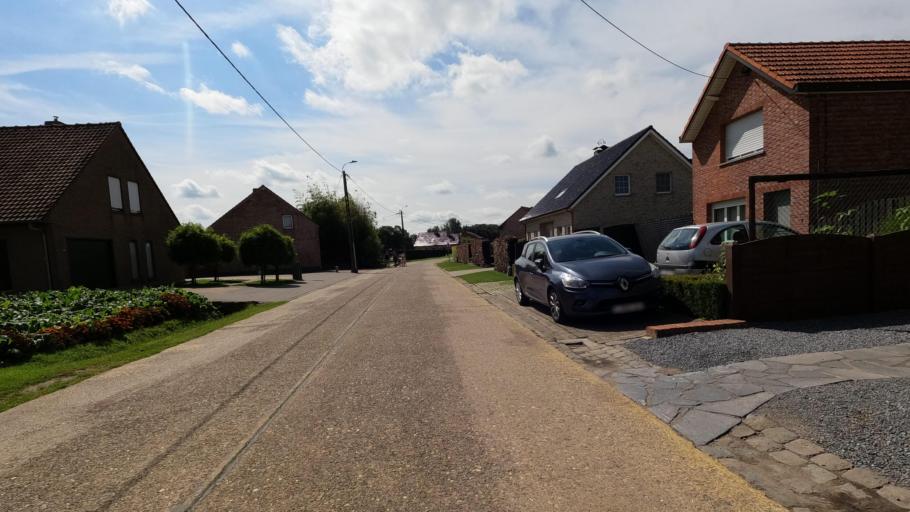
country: BE
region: Flanders
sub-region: Provincie Antwerpen
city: Heist-op-den-Berg
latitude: 51.0684
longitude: 4.7489
